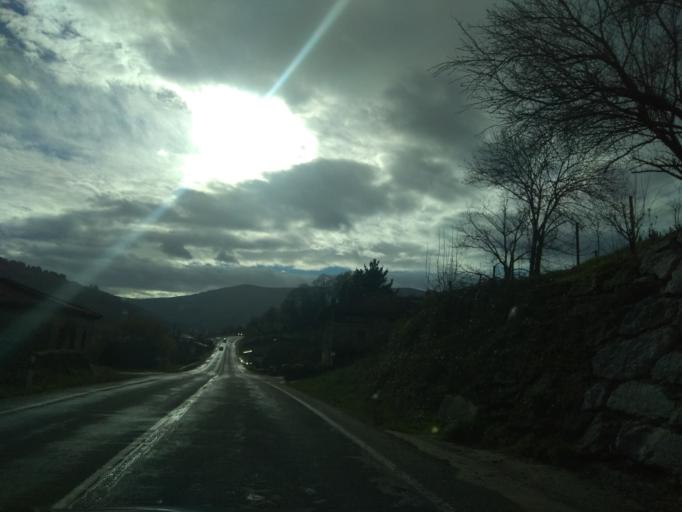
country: ES
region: Cantabria
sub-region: Provincia de Cantabria
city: San Pedro del Romeral
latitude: 43.1267
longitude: -3.9014
